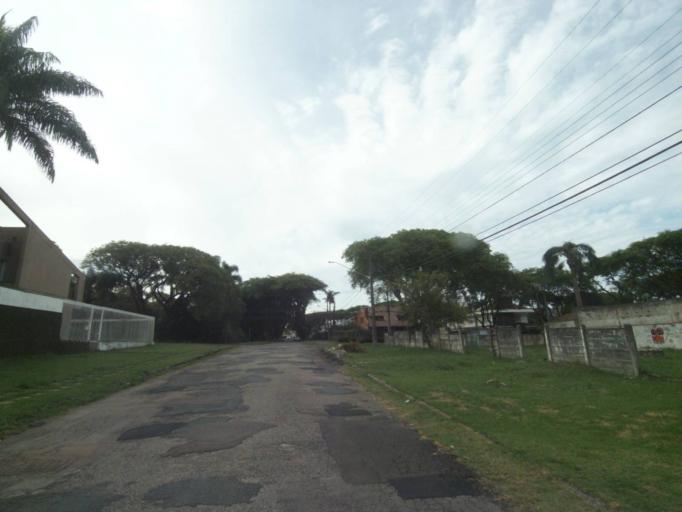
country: BR
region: Parana
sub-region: Pinhais
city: Pinhais
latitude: -25.4240
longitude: -49.2298
